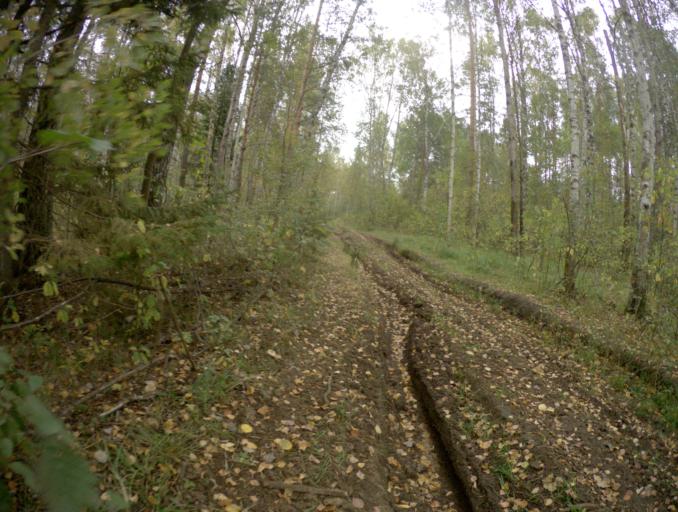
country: RU
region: Moskovskaya
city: Misheronskiy
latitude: 55.7752
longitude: 39.6056
